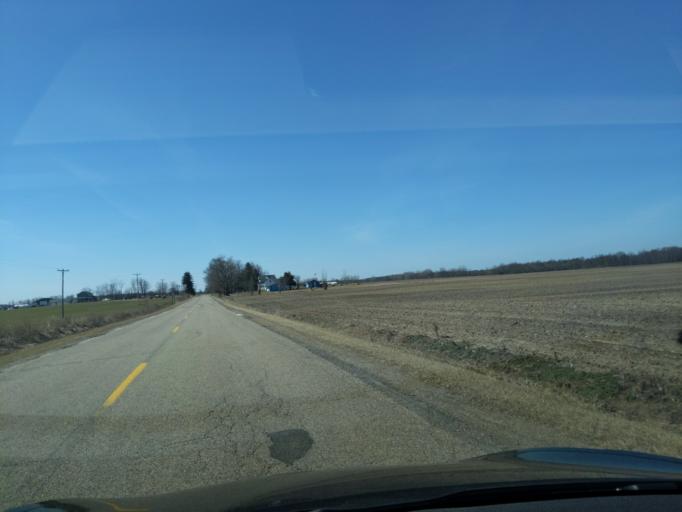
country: US
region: Michigan
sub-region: Ionia County
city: Portland
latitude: 42.7266
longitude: -84.9359
